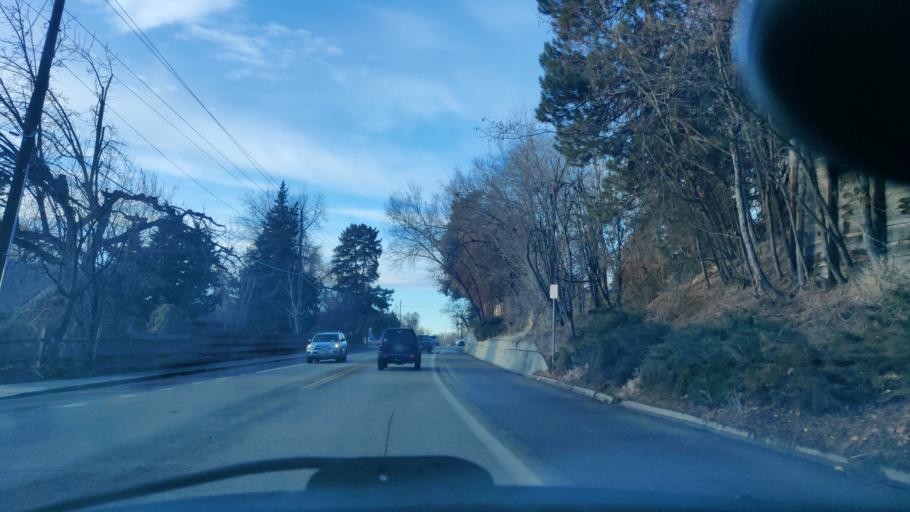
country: US
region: Idaho
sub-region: Ada County
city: Boise
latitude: 43.6426
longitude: -116.2132
